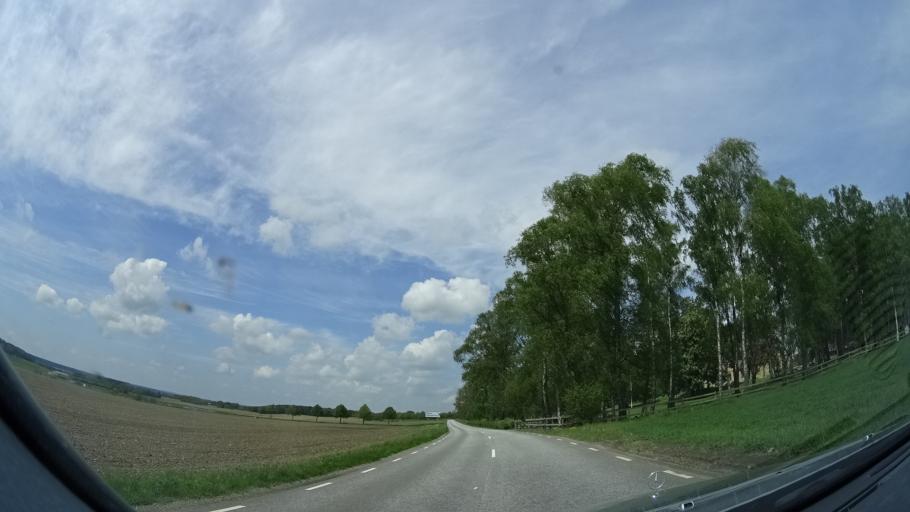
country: SE
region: Skane
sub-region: Sjobo Kommun
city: Sjoebo
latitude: 55.6767
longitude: 13.6570
